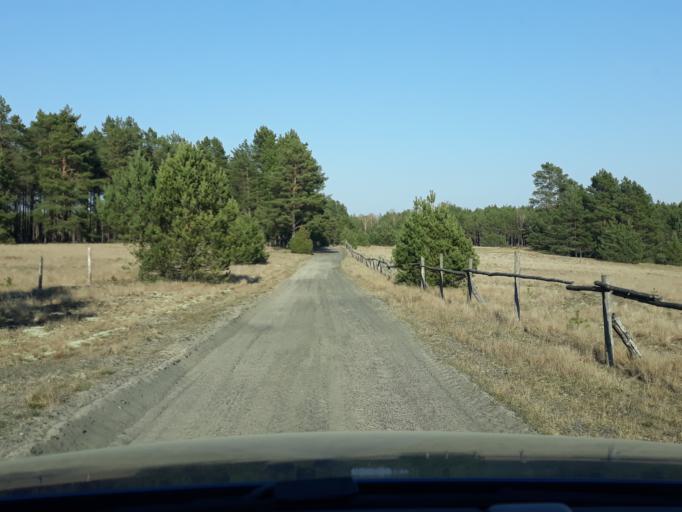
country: PL
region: Pomeranian Voivodeship
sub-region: Powiat bytowski
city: Lipnica
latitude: 53.8993
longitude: 17.4193
